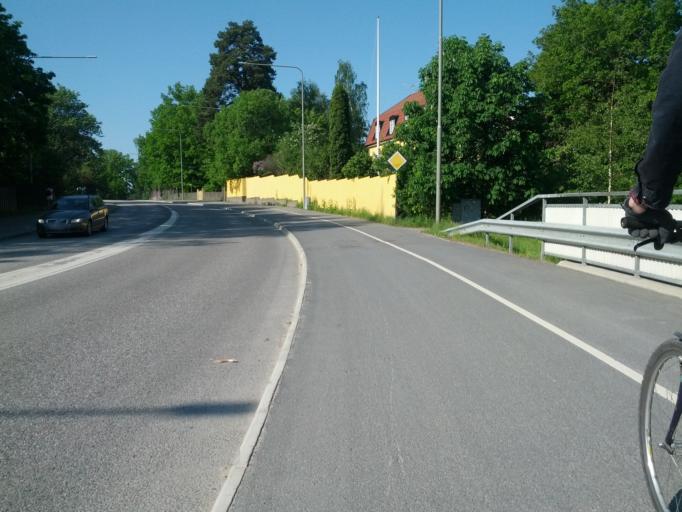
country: SE
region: Stockholm
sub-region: Danderyds Kommun
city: Djursholm
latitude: 59.3990
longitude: 18.0551
